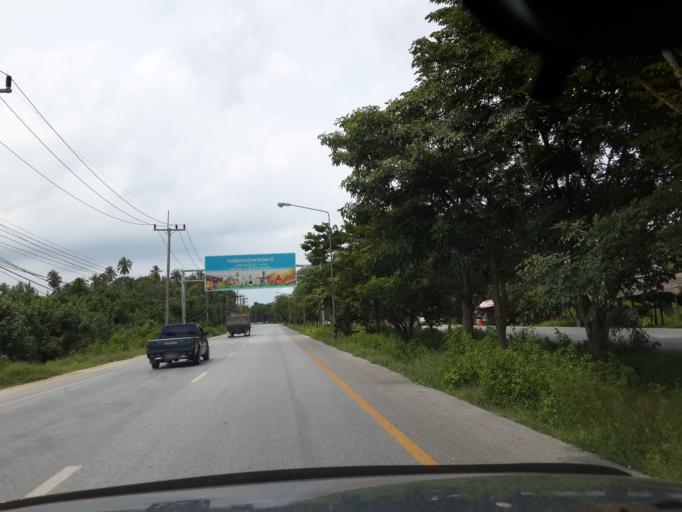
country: TH
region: Pattani
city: Yaring
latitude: 6.8706
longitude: 101.3197
